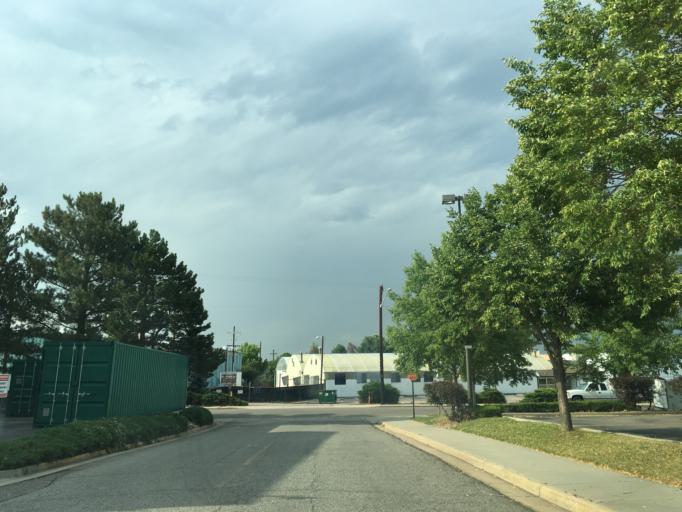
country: US
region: Colorado
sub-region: Jefferson County
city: Lakewood
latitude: 39.6787
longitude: -105.0559
